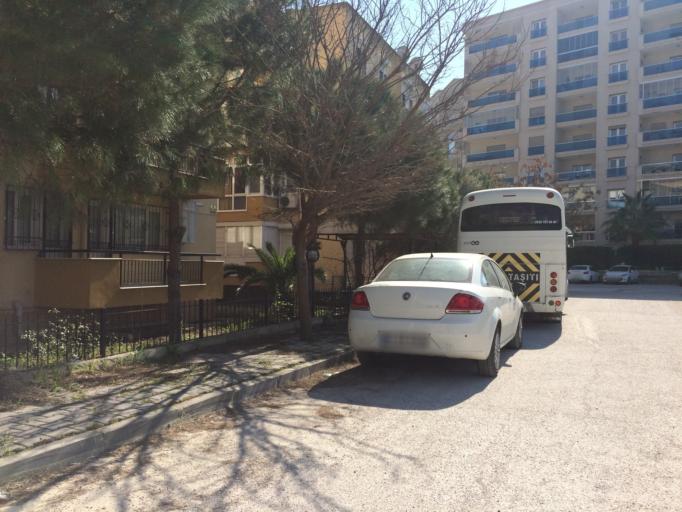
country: TR
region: Izmir
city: Karsiyaka
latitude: 38.4875
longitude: 27.0599
